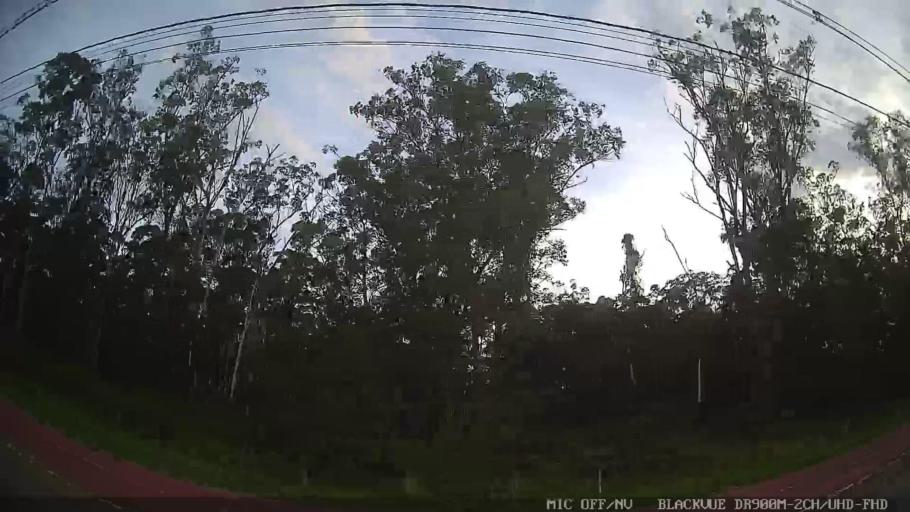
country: BR
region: Sao Paulo
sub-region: Mogi das Cruzes
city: Mogi das Cruzes
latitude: -23.4996
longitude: -46.1704
